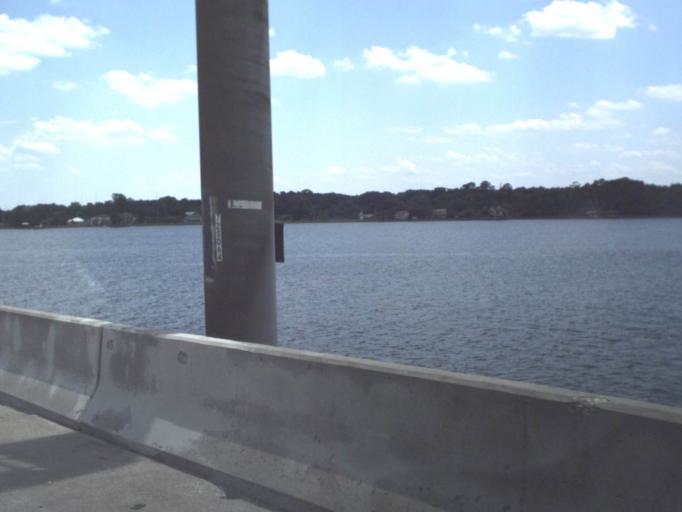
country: US
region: Florida
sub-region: Duval County
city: Jacksonville
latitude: 30.3741
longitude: -81.5526
